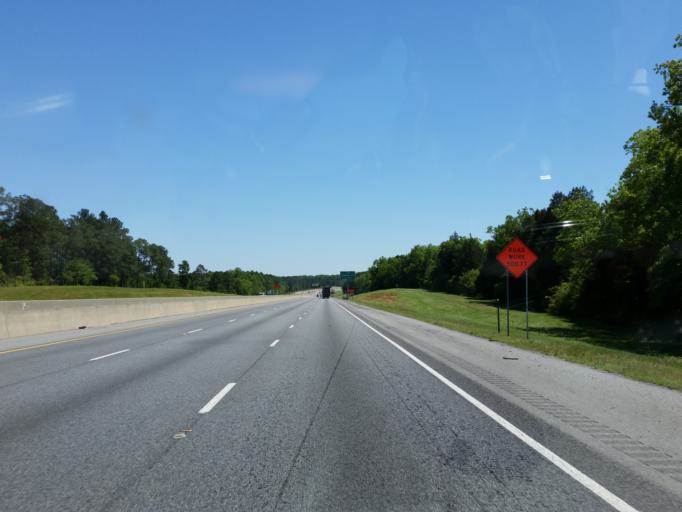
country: US
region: Georgia
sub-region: Tift County
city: Tifton
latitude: 31.5242
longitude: -83.5207
